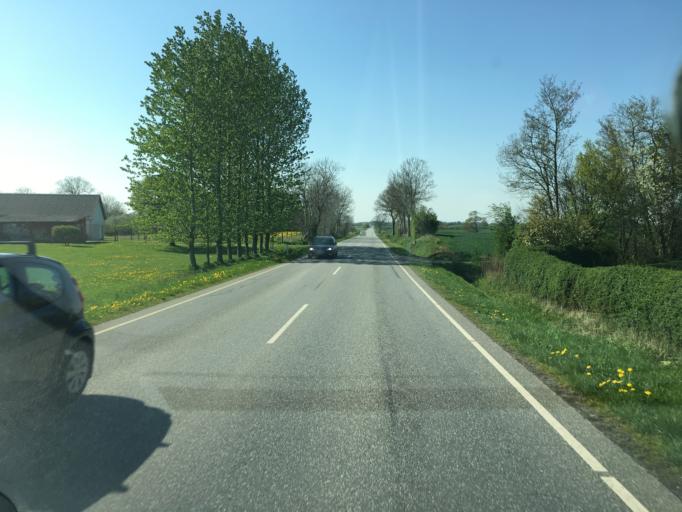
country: DK
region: South Denmark
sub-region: Haderslev Kommune
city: Vojens
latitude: 55.3079
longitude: 9.3478
